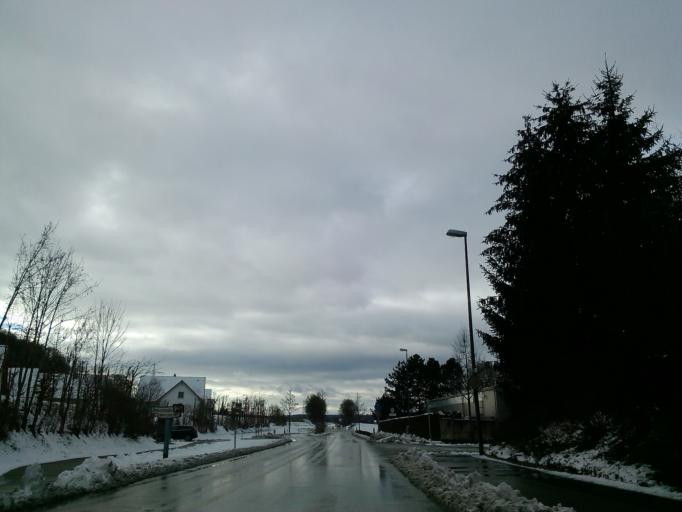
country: DE
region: Bavaria
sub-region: Swabia
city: Zusmarshausen
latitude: 48.3941
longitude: 10.5950
